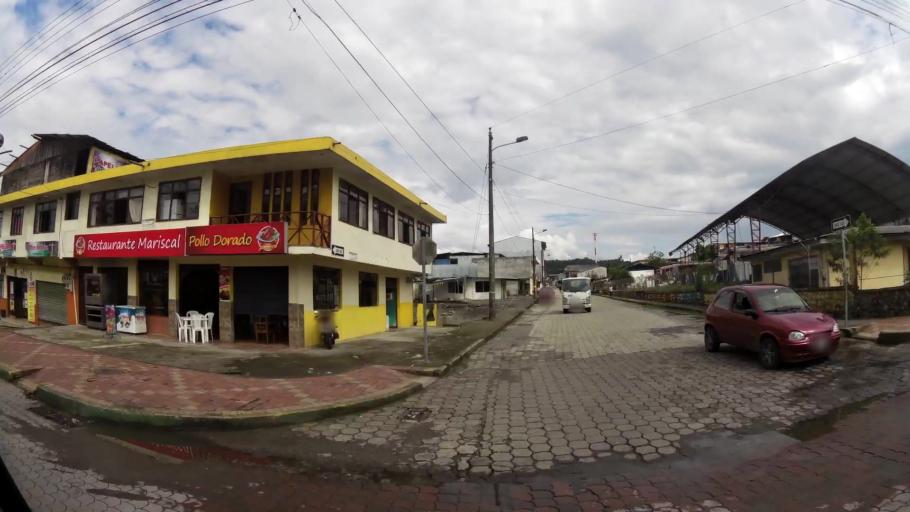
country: EC
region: Pastaza
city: Puyo
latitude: -1.4876
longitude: -78.0075
